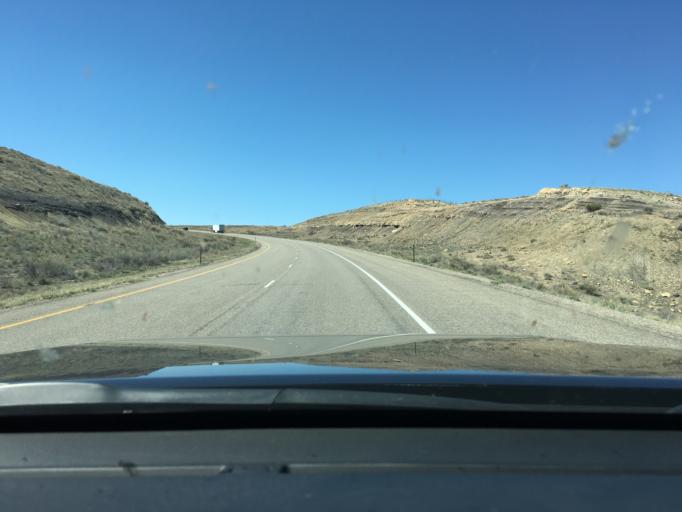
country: US
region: Colorado
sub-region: Mesa County
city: Loma
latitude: 39.2319
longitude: -108.9038
